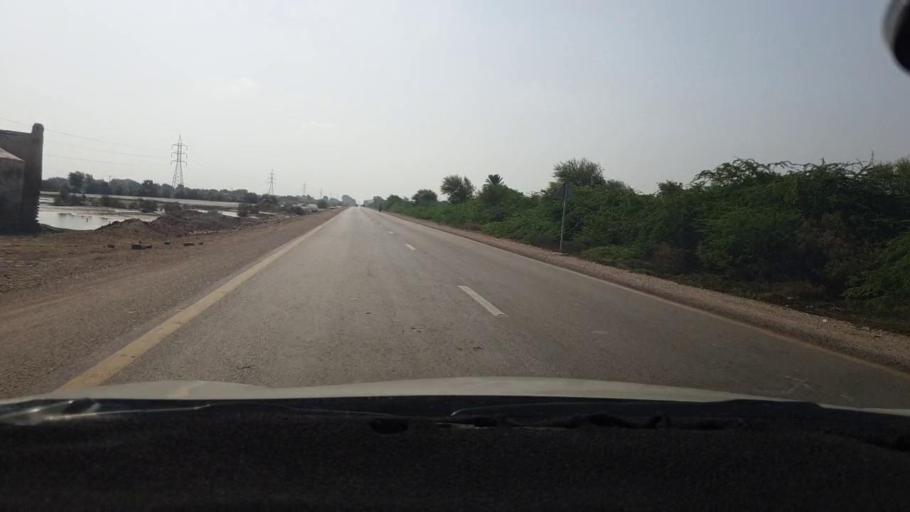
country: PK
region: Sindh
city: Jhol
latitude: 25.9111
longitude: 69.0131
